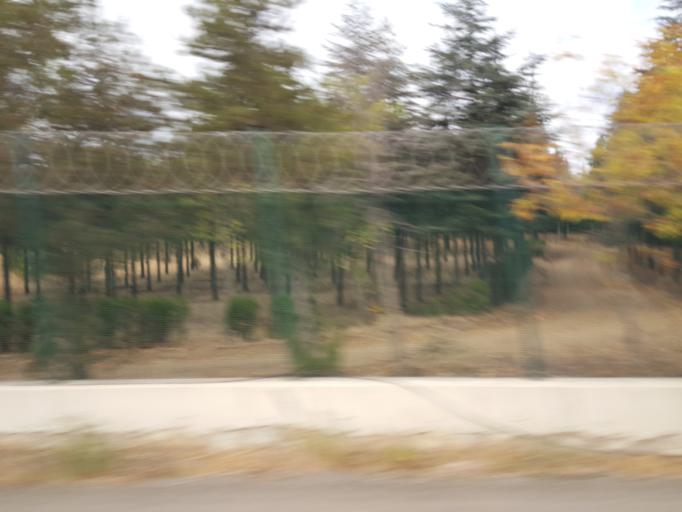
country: TR
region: Kirikkale
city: Bahsili
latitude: 39.7599
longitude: 33.4579
